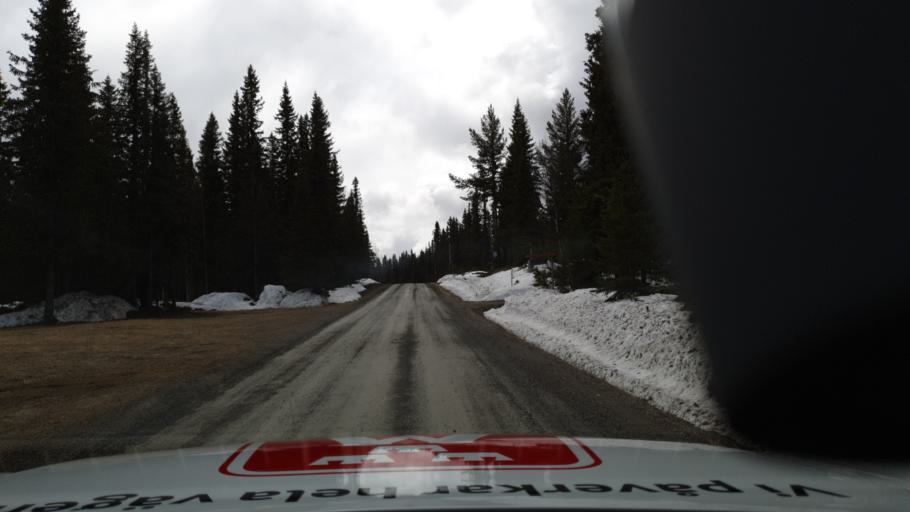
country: SE
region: Jaemtland
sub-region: Are Kommun
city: Jarpen
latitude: 62.8357
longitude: 13.8191
